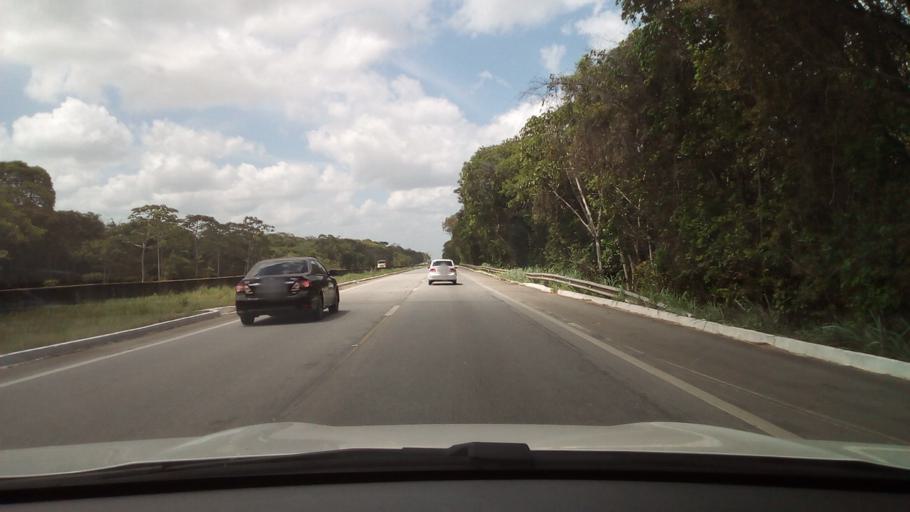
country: BR
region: Paraiba
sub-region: Mamanguape
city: Mamanguape
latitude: -6.9835
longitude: -35.0745
